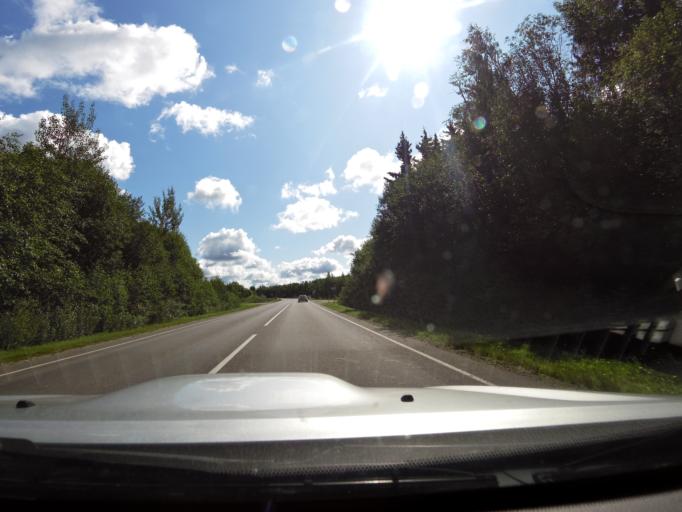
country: LT
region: Utenos apskritis
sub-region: Utena
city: Utena
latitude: 55.4860
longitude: 25.6367
